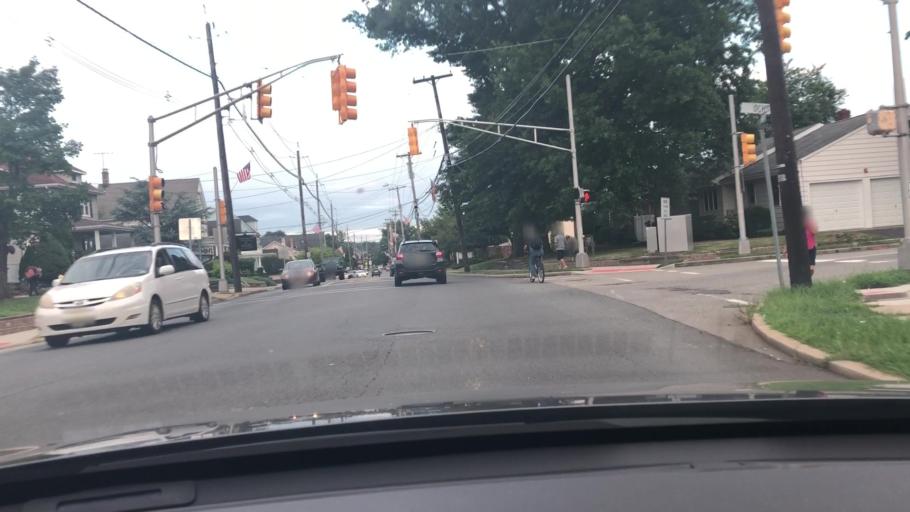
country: US
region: New Jersey
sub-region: Middlesex County
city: Milltown
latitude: 40.4561
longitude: -74.4439
